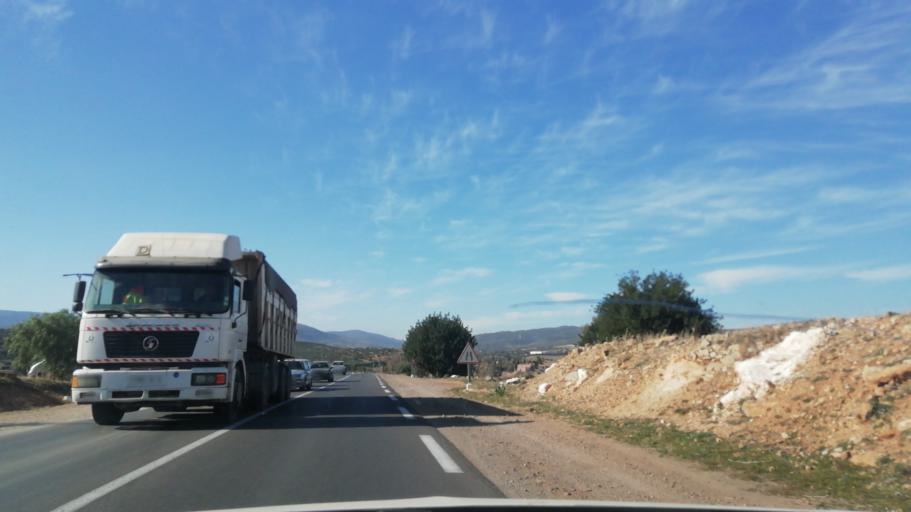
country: DZ
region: Tlemcen
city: Ouled Mimoun
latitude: 34.8689
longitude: -1.1305
